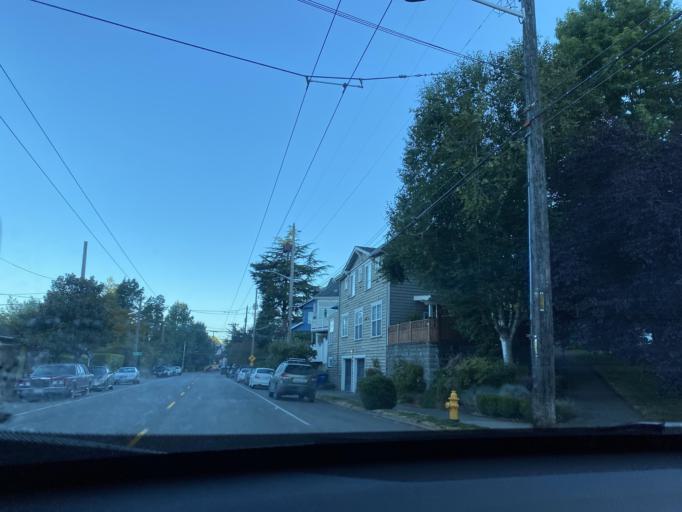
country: US
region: Washington
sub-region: King County
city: Seattle
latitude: 47.6301
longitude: -122.3691
